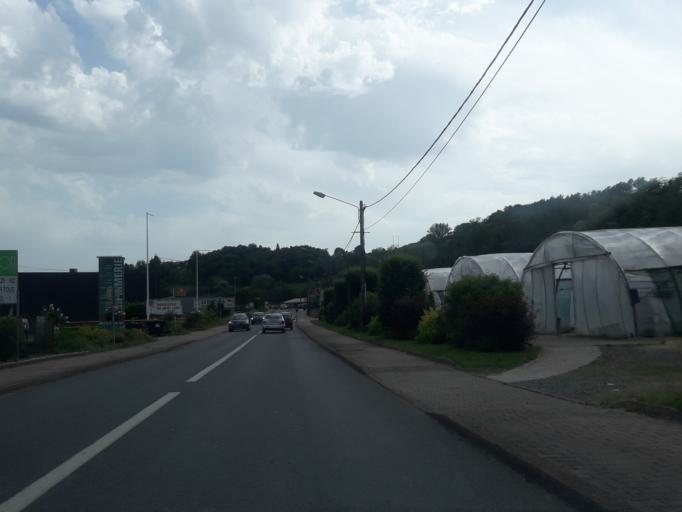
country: FR
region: Rhone-Alpes
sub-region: Departement du Rhone
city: Sain-Bel
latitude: 45.8271
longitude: 4.6080
